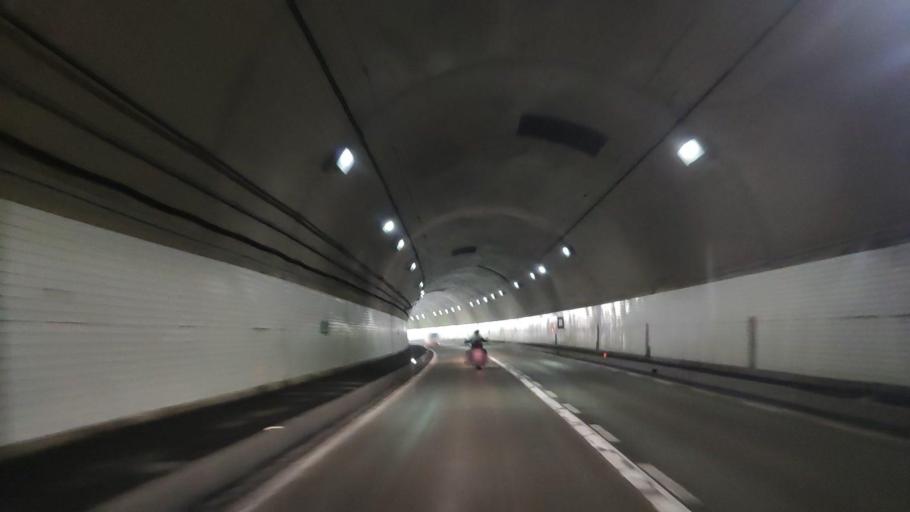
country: JP
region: Akita
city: Yuzawa
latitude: 39.0017
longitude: 140.3664
